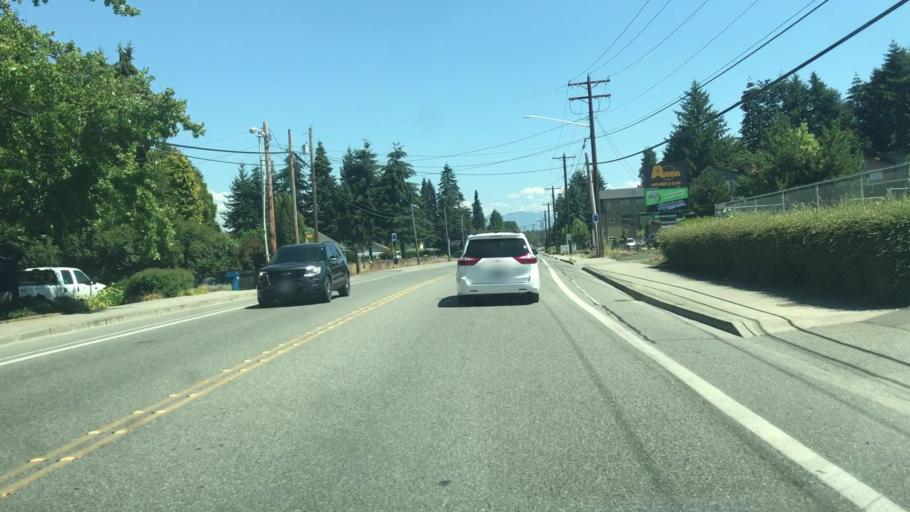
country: US
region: Washington
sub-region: Snohomish County
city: Monroe
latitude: 47.8504
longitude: -121.9982
